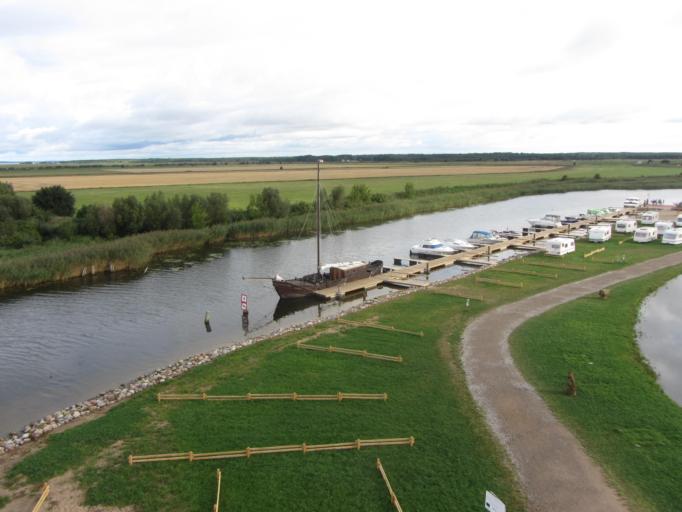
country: LT
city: Priekule
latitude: 55.5173
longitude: 21.2366
